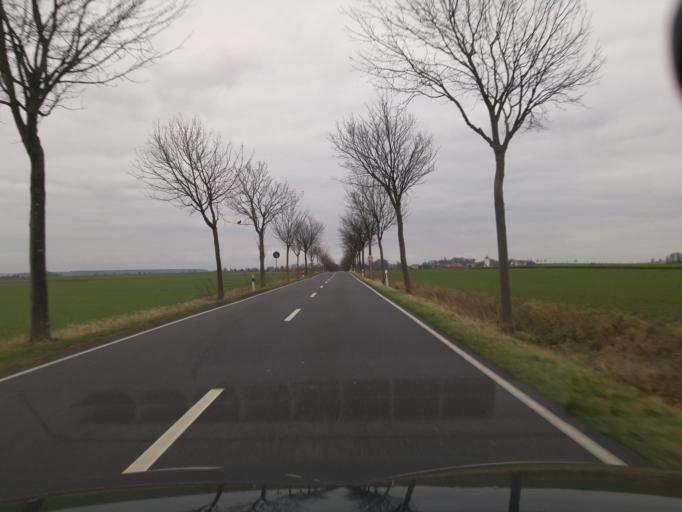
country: DE
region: Lower Saxony
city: Ilsede
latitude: 52.2257
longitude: 10.1754
